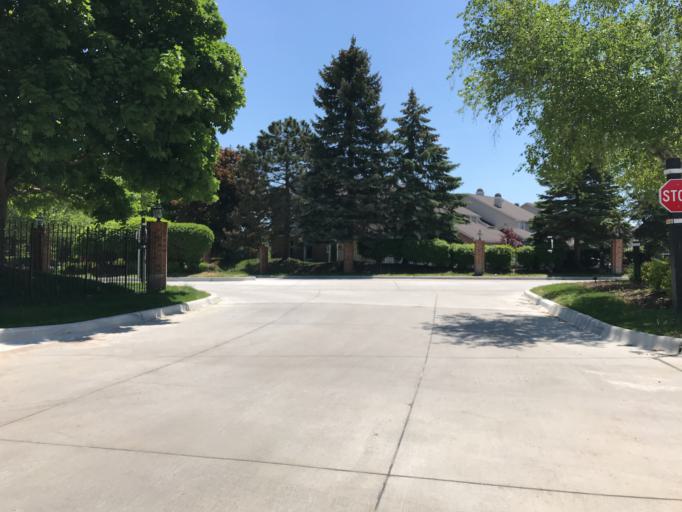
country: US
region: Michigan
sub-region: Oakland County
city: West Bloomfield Township
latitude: 42.5392
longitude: -83.3652
